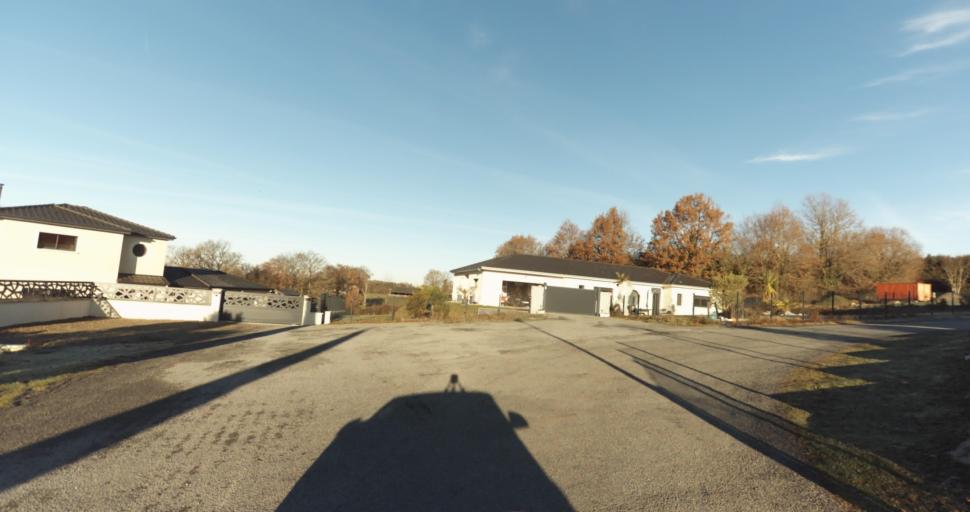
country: FR
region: Limousin
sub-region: Departement de la Haute-Vienne
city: Aixe-sur-Vienne
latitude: 45.8122
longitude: 1.1476
